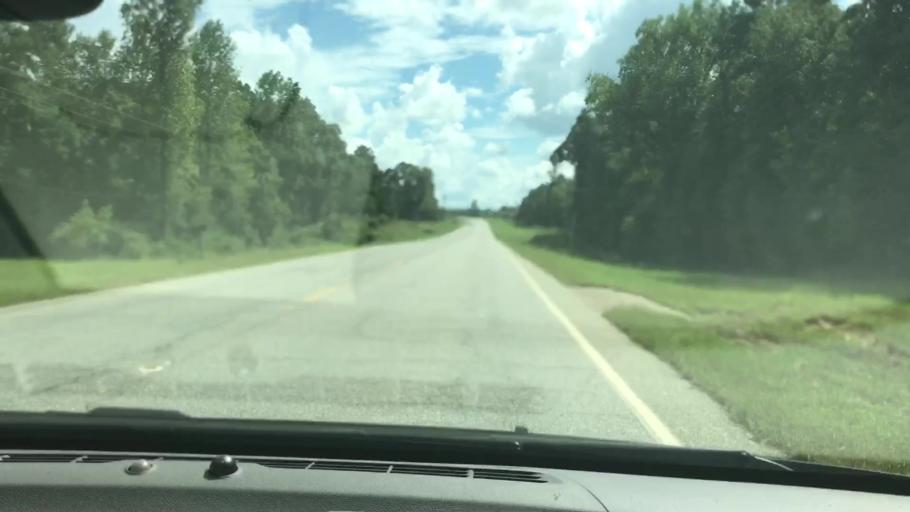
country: US
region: Georgia
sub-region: Clay County
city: Fort Gaines
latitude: 31.6800
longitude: -85.0470
